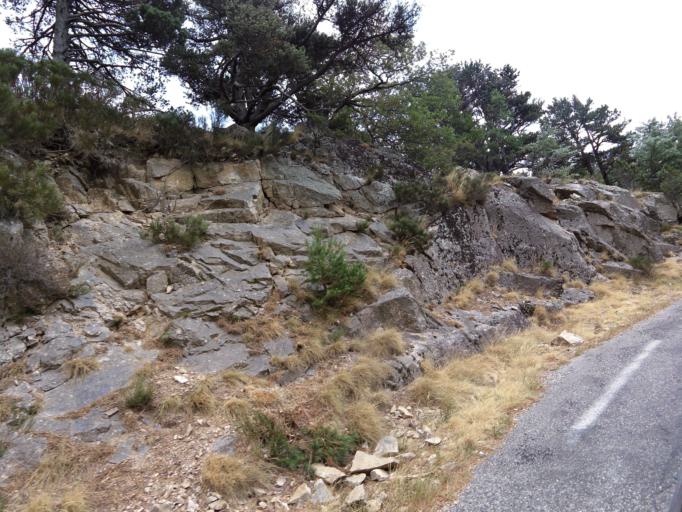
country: FR
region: Languedoc-Roussillon
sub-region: Departement du Gard
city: Valleraugue
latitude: 44.0452
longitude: 3.6083
